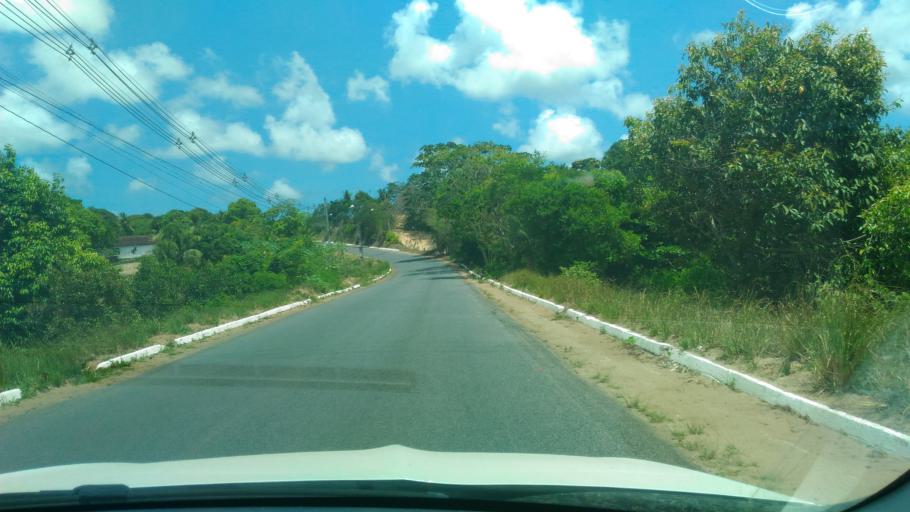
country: BR
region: Paraiba
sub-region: Conde
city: Conde
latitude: -7.2631
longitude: -34.9240
